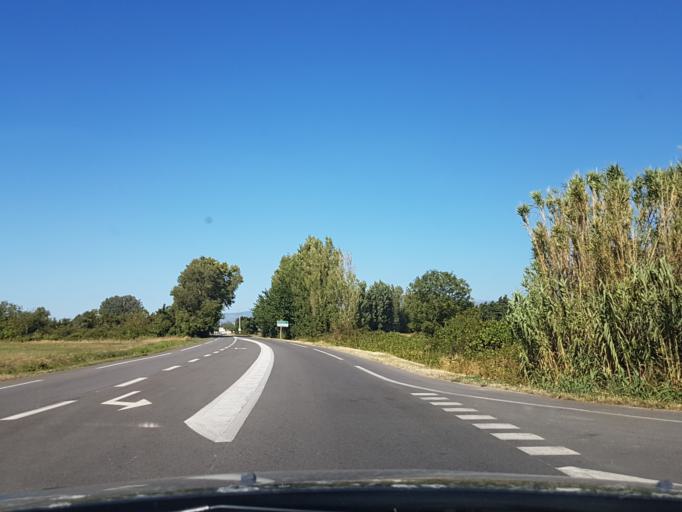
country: FR
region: Provence-Alpes-Cote d'Azur
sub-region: Departement du Vaucluse
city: Pernes-les-Fontaines
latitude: 44.0018
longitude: 5.0164
